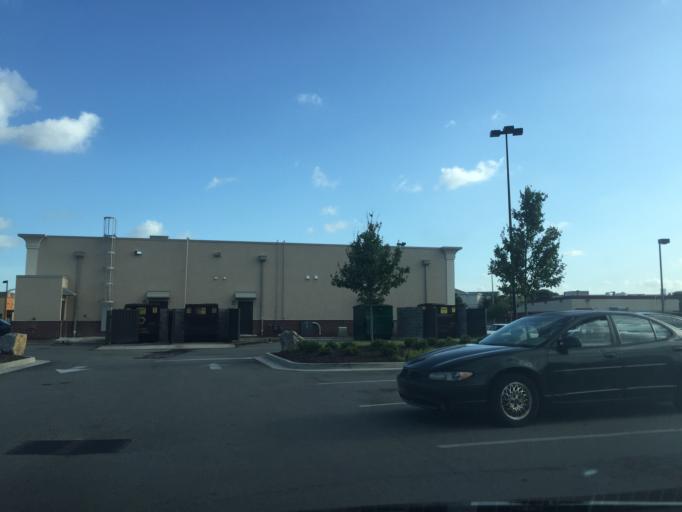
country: US
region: Georgia
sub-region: Chatham County
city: Isle of Hope
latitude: 32.0058
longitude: -81.1138
